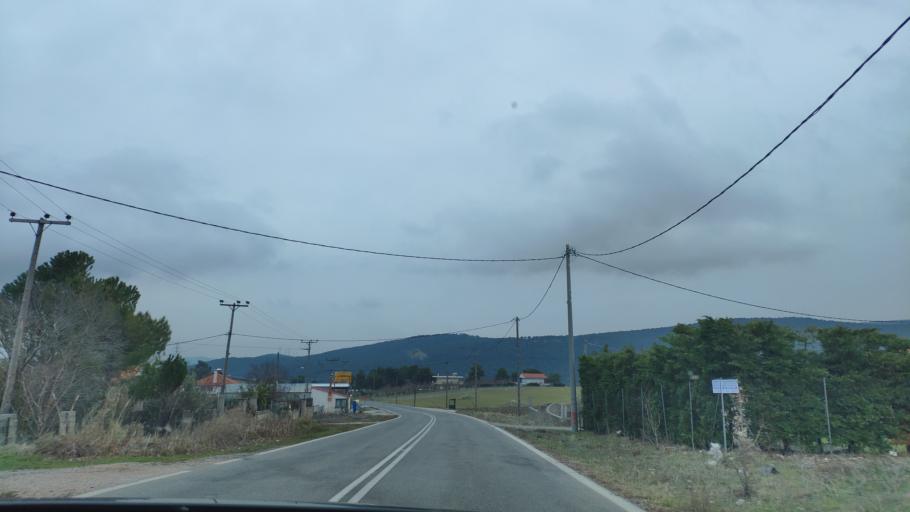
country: GR
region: Attica
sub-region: Nomarchia Dytikis Attikis
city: Vilia
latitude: 38.1738
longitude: 23.3850
